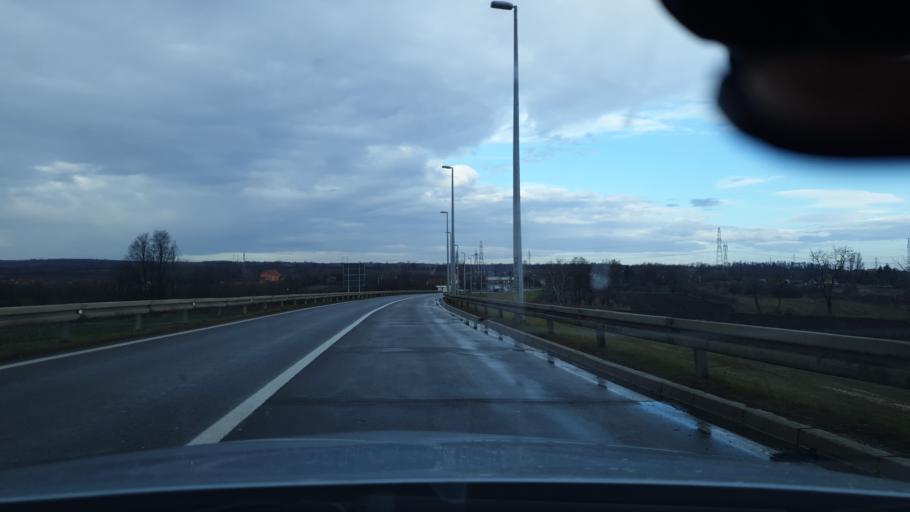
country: RS
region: Central Serbia
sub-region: Podunavski Okrug
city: Smederevo
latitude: 44.5873
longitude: 20.9587
